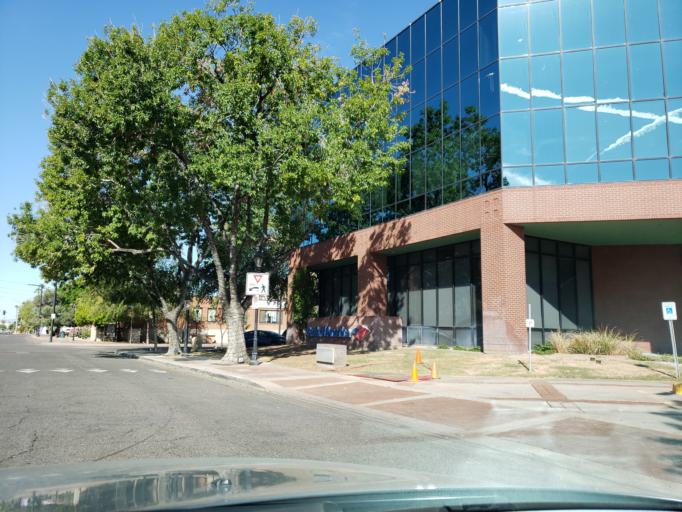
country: US
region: Arizona
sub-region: Maricopa County
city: Glendale
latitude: 33.5399
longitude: -112.1844
